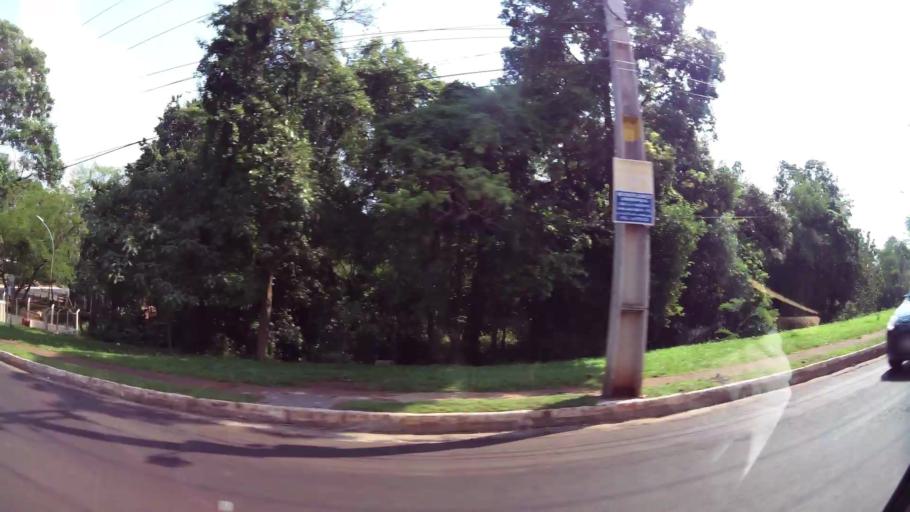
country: PY
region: Alto Parana
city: Ciudad del Este
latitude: -25.5164
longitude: -54.6233
